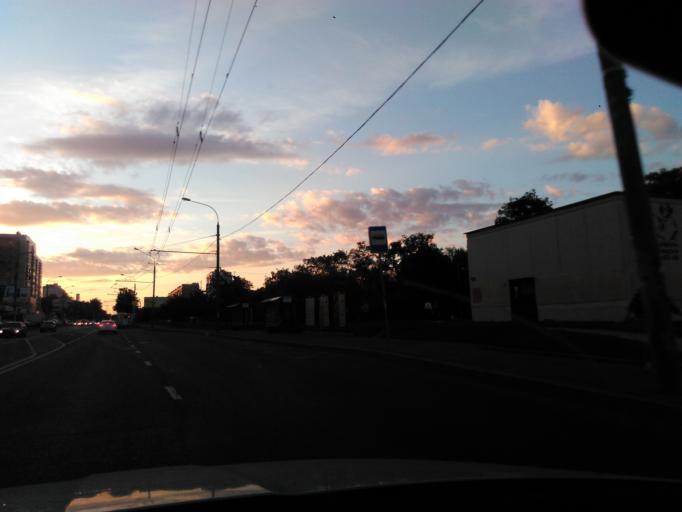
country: RU
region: Moscow
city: Zapadnoye Degunino
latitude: 55.8752
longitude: 37.5261
